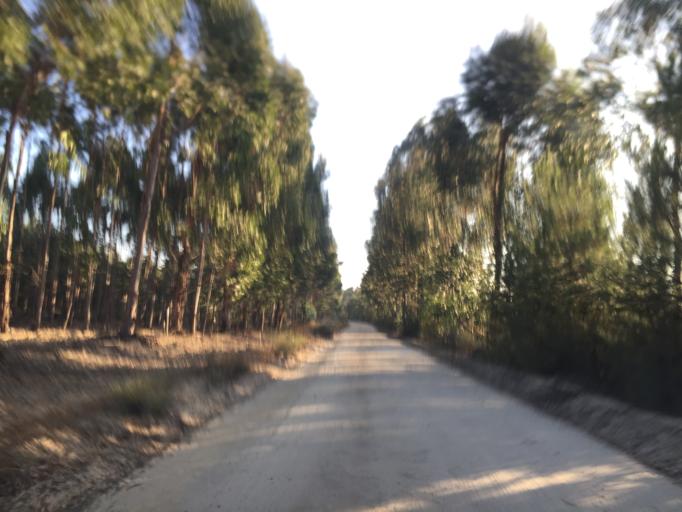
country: PT
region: Portalegre
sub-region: Ponte de Sor
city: Santo Andre
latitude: 39.1324
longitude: -8.3189
